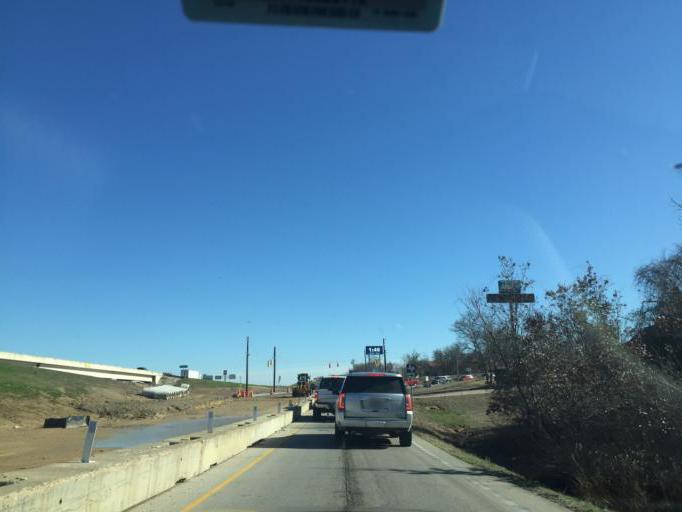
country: US
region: Texas
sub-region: Parker County
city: Willow Park
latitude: 32.7473
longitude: -97.6752
